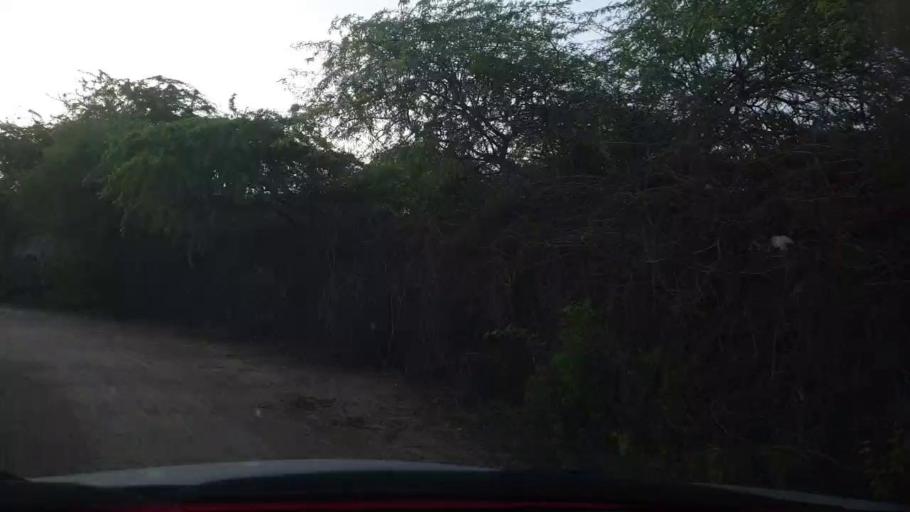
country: PK
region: Sindh
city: Talhar
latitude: 24.9276
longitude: 68.8260
